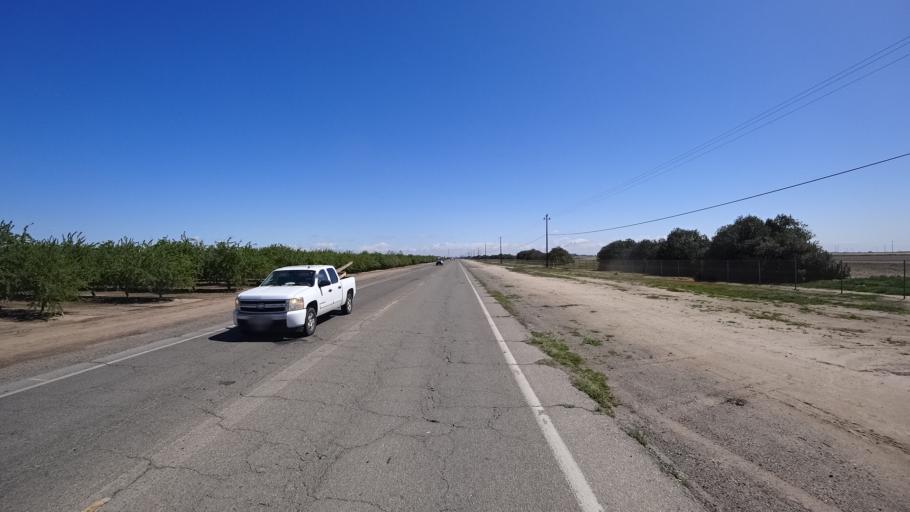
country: US
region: California
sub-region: Fresno County
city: West Park
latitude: 36.7063
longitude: -119.9141
